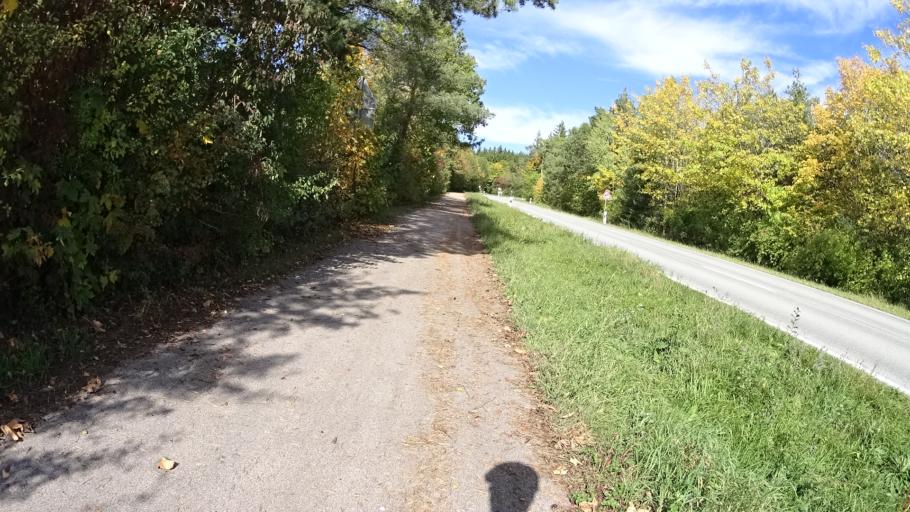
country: DE
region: Bavaria
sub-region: Upper Bavaria
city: Bohmfeld
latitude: 48.8403
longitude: 11.3703
